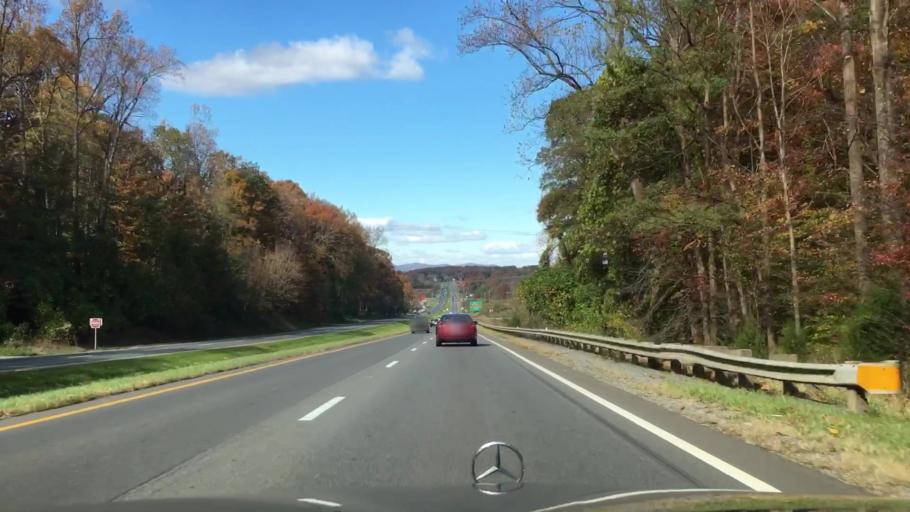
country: US
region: Virginia
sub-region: Campbell County
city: Rustburg
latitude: 37.3024
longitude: -79.1758
